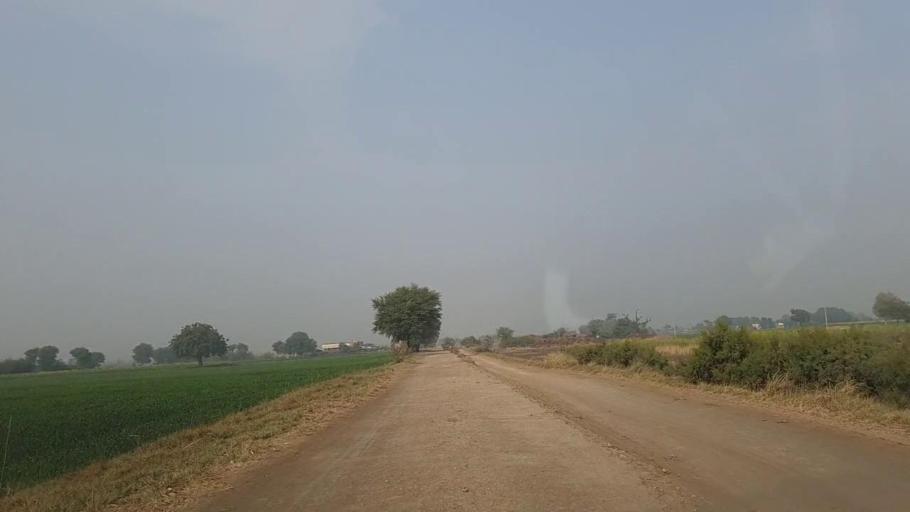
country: PK
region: Sindh
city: Sanghar
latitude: 26.1046
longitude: 68.8963
